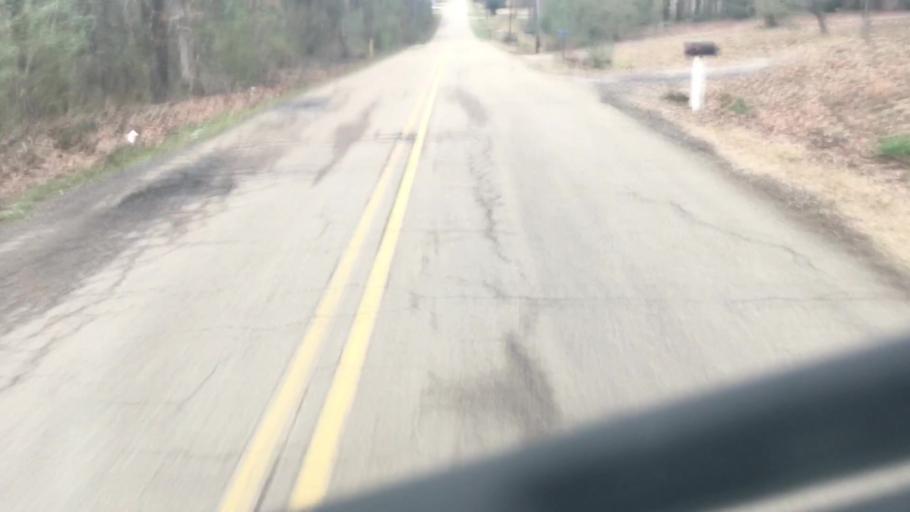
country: US
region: Alabama
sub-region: Walker County
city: Jasper
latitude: 33.8307
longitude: -87.2253
